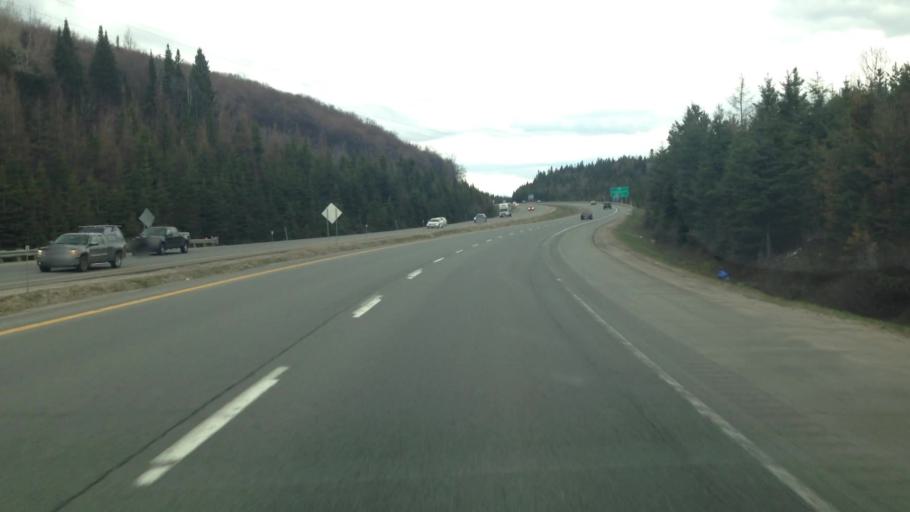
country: CA
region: Quebec
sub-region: Laurentides
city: Sainte-Agathe-des-Monts
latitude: 46.0282
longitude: -74.2627
